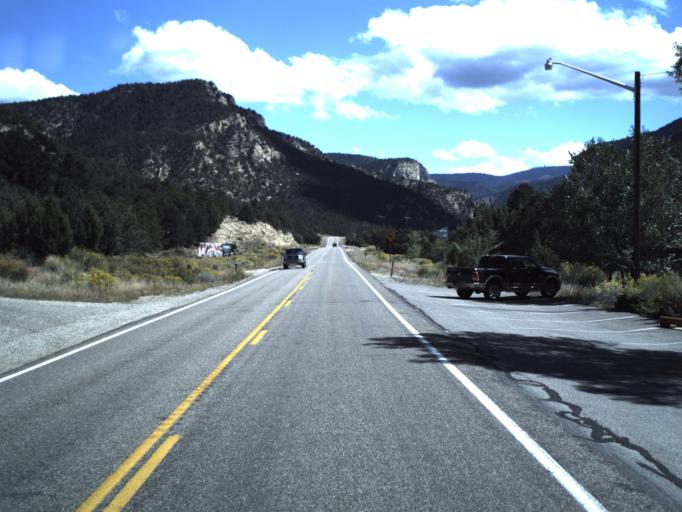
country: US
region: Utah
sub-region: Iron County
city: Cedar City
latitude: 37.6526
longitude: -112.9843
